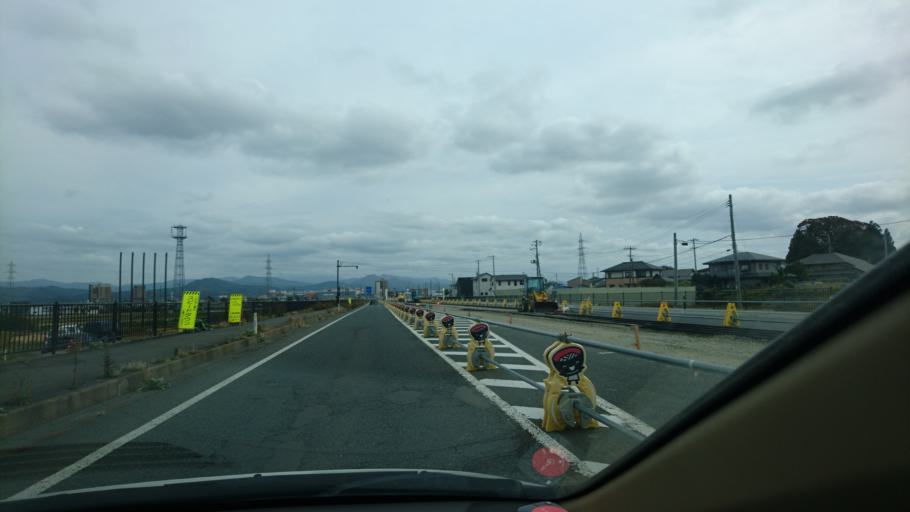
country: JP
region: Iwate
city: Morioka-shi
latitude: 39.6893
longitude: 141.1130
